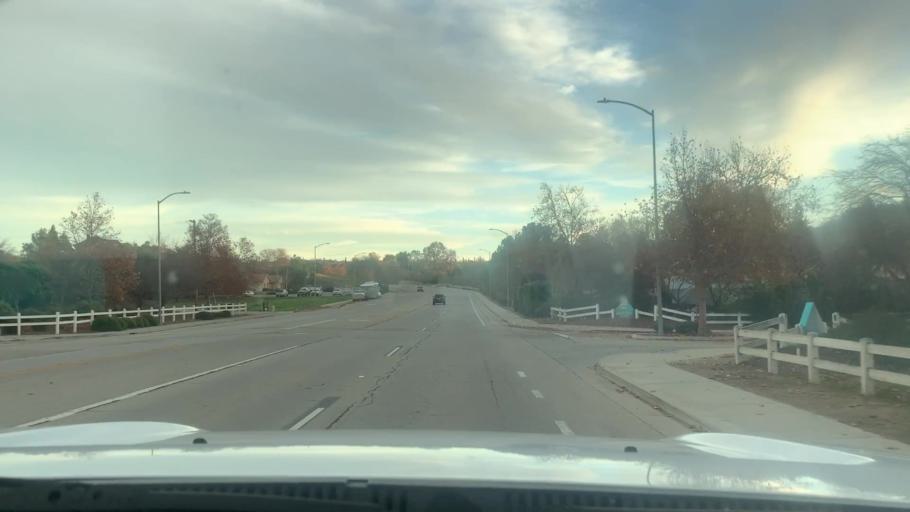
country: US
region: California
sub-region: San Luis Obispo County
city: Paso Robles
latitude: 35.6371
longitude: -120.6582
